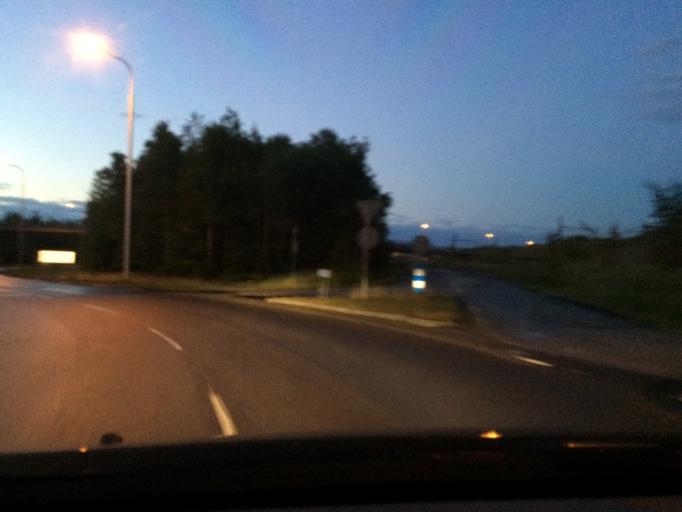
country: SE
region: Skane
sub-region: Malmo
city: Bunkeflostrand
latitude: 55.5561
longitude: 12.9554
